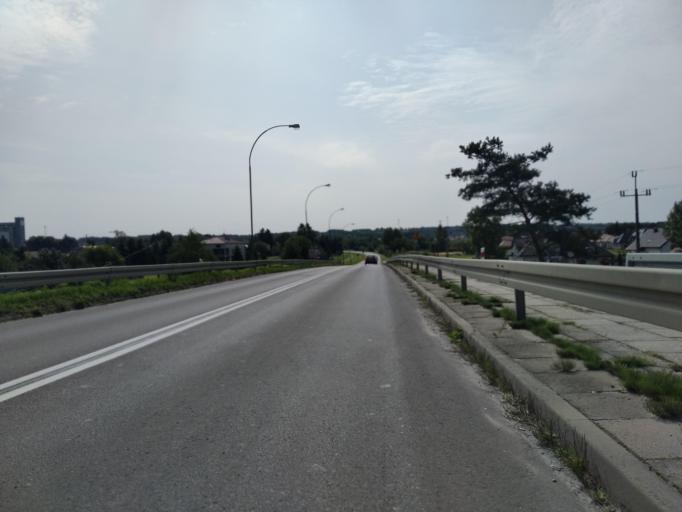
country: PL
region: Subcarpathian Voivodeship
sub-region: Powiat ropczycko-sedziszowski
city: Ostrow
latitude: 50.0779
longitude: 21.5836
